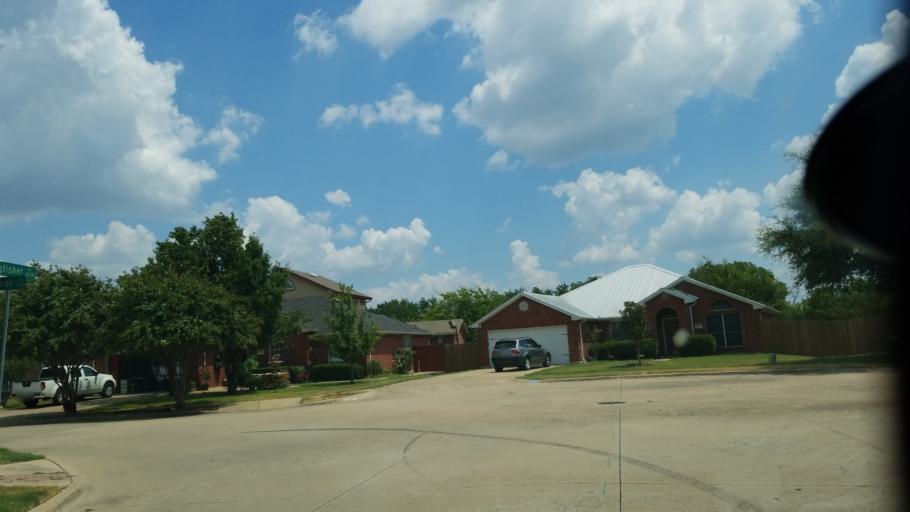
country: US
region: Texas
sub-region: Dallas County
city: Duncanville
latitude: 32.6794
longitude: -96.8955
